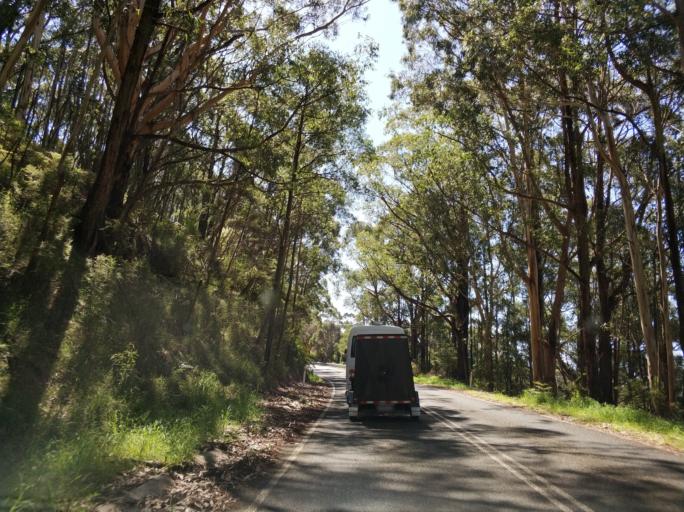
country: AU
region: Victoria
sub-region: Colac-Otway
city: Apollo Bay
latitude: -38.7468
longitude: 143.2750
